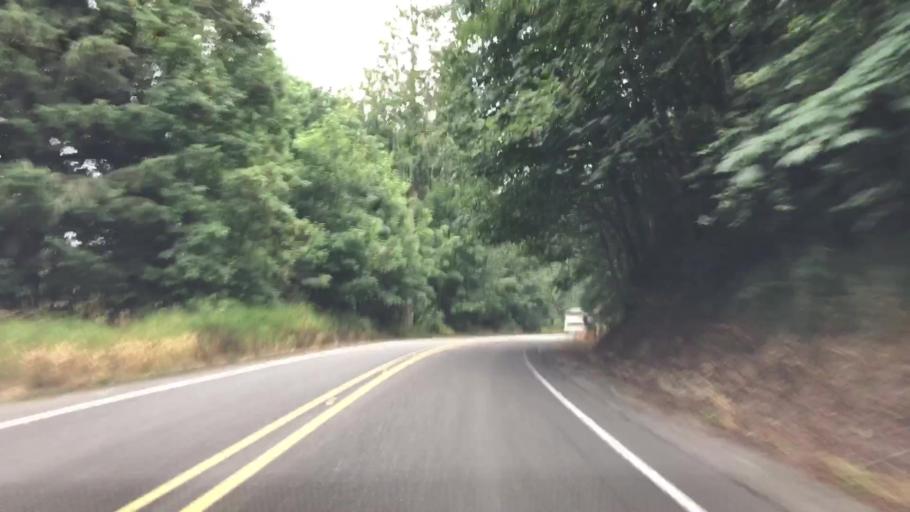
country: US
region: Washington
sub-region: Kitsap County
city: Navy Yard City
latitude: 47.5254
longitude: -122.7409
